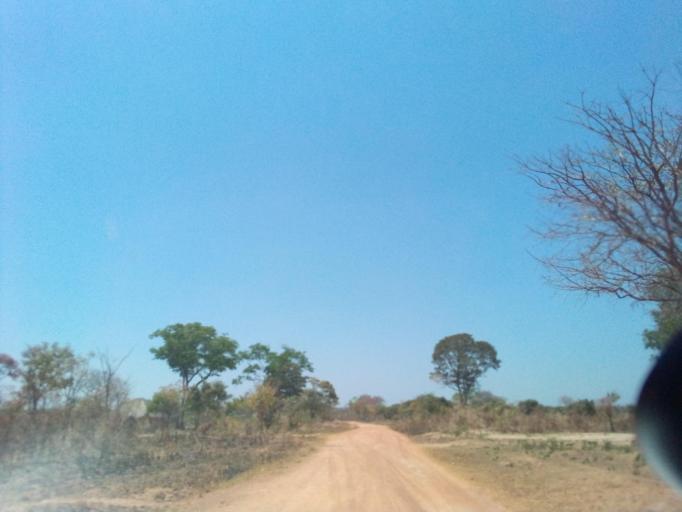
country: ZM
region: Northern
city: Mpika
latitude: -12.2519
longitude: 30.6748
